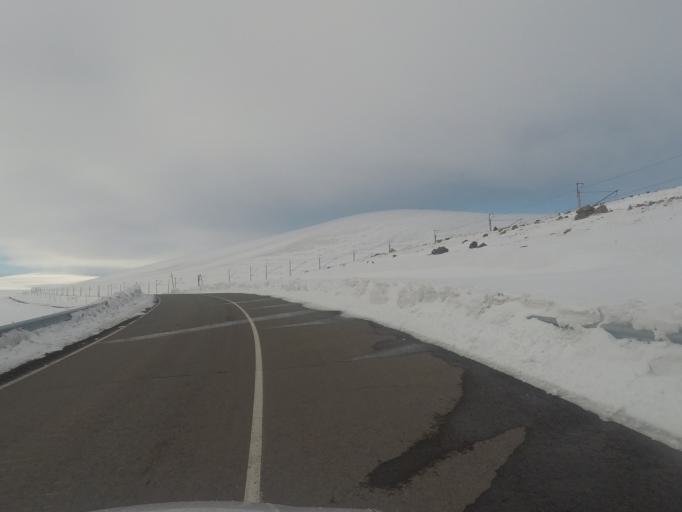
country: GE
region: Kvemo Kartli
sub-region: Tsalka
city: Tsalka
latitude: 41.4627
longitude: 43.8613
